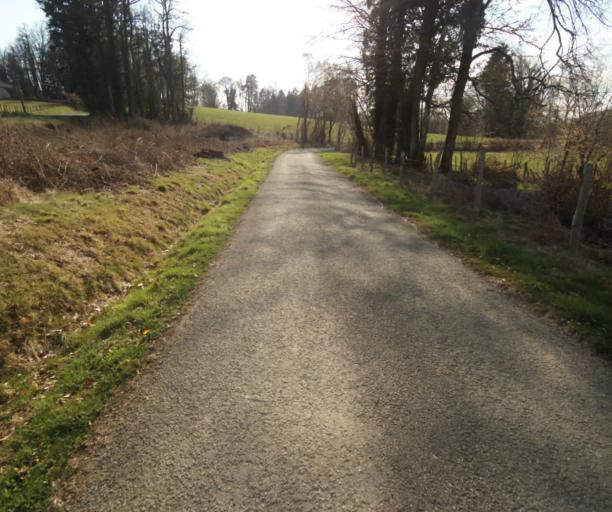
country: FR
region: Limousin
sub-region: Departement de la Correze
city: Saint-Mexant
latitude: 45.3353
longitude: 1.6140
